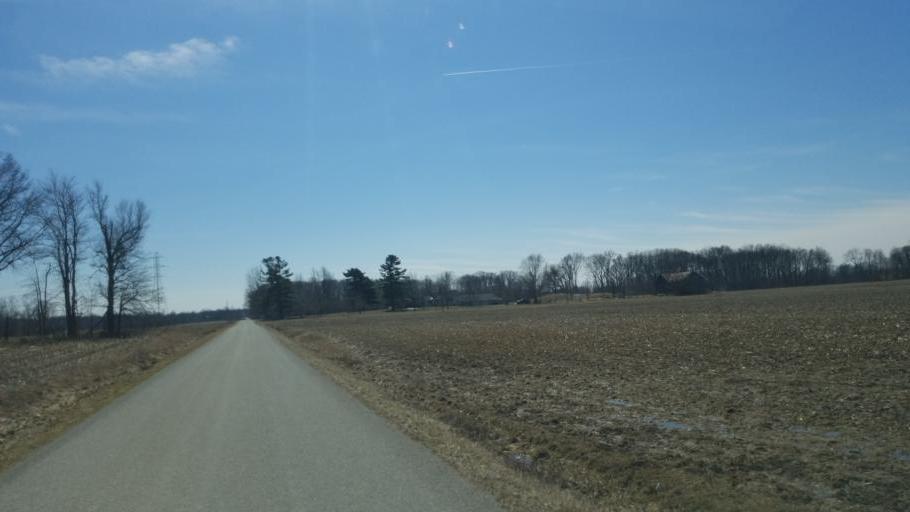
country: US
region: Ohio
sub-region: Crawford County
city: Galion
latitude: 40.7080
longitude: -82.7556
